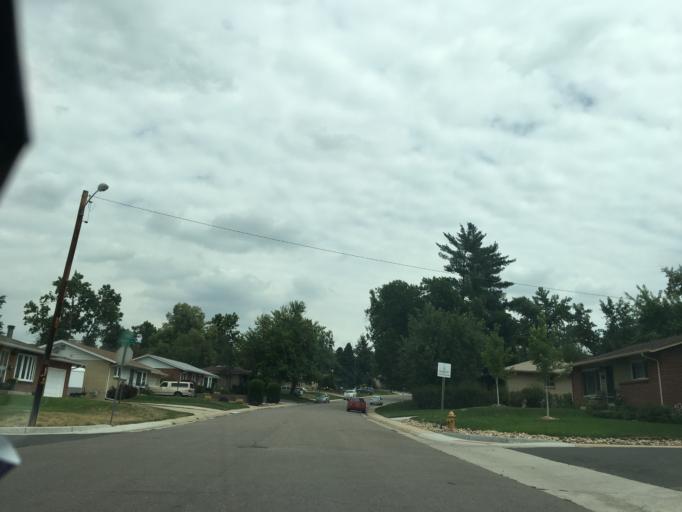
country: US
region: Colorado
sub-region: Arapahoe County
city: Sheridan
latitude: 39.6623
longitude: -105.0429
